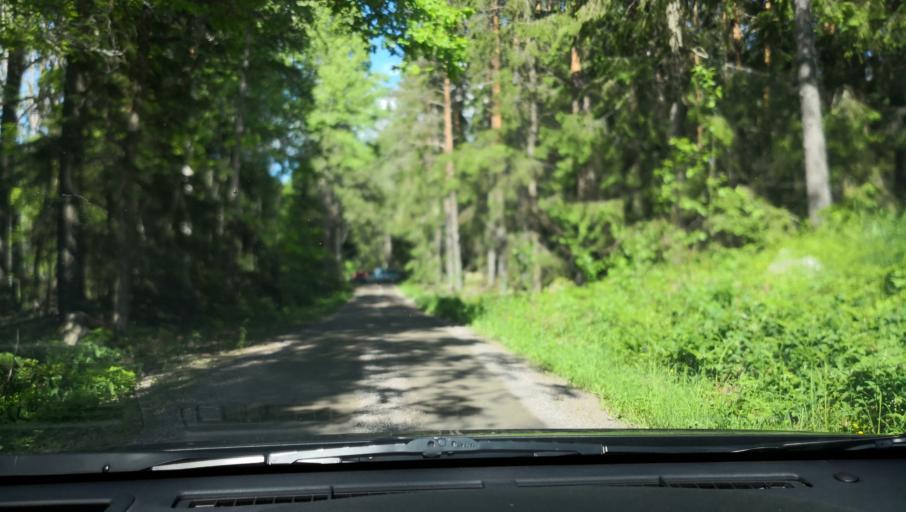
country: SE
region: Vaestmanland
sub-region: Arboga Kommun
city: Tyringe
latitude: 59.3195
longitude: 16.0006
